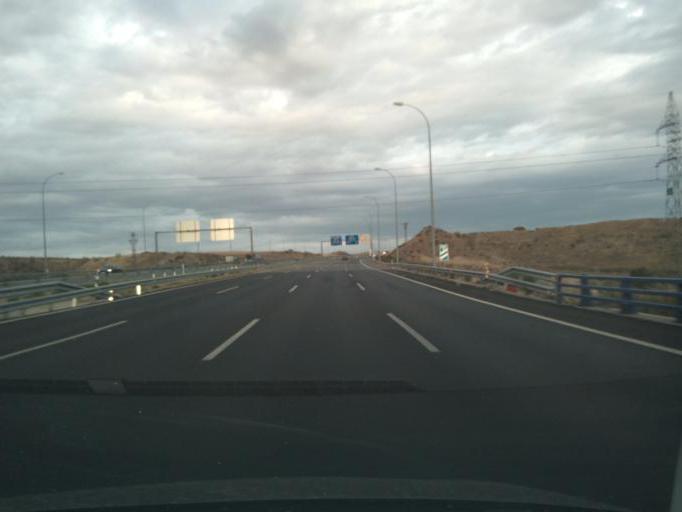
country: ES
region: Madrid
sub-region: Provincia de Madrid
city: Paracuellos de Jarama
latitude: 40.5440
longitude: -3.5497
